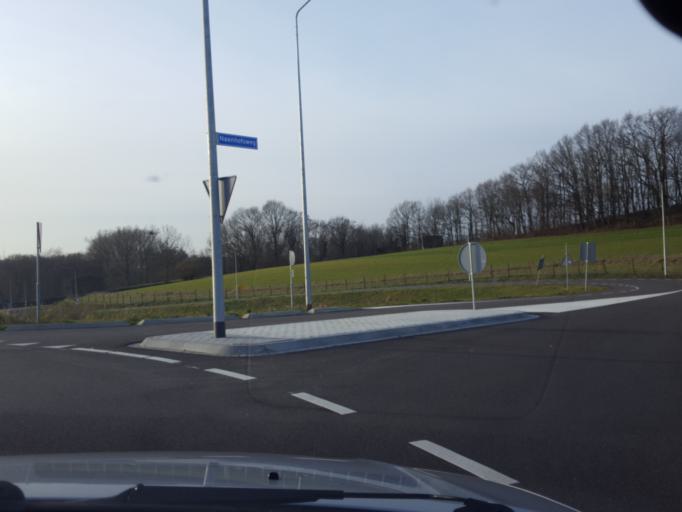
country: NL
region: Limburg
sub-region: Gemeente Nuth
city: Nuth
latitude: 50.9243
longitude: 5.9040
